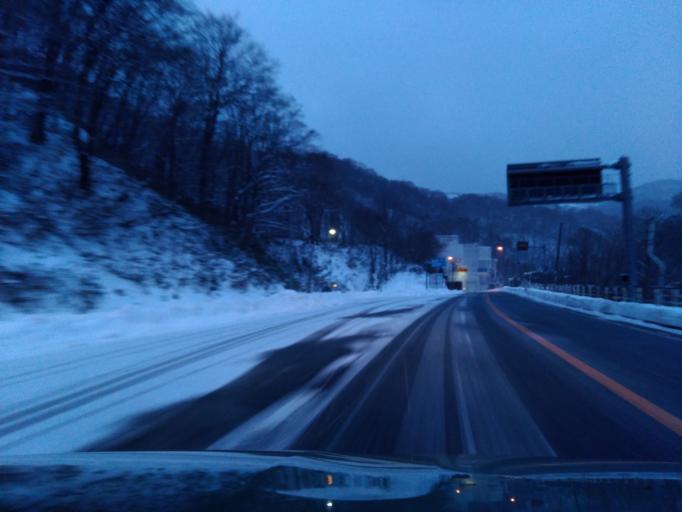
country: JP
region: Iwate
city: Shizukuishi
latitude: 39.7175
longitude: 140.8203
